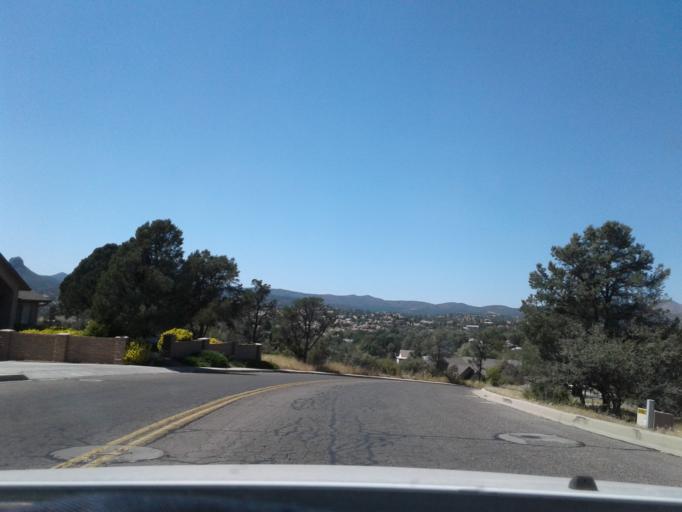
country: US
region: Arizona
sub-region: Yavapai County
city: Prescott
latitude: 34.5691
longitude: -112.4698
